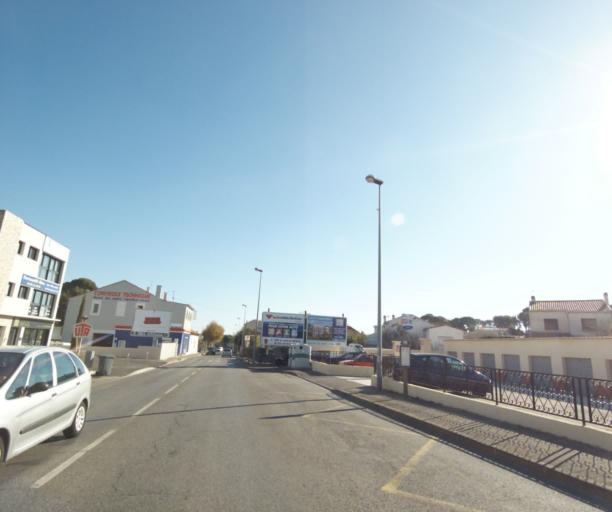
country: FR
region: Provence-Alpes-Cote d'Azur
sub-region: Departement des Bouches-du-Rhone
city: La Ciotat
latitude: 43.1851
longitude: 5.6085
